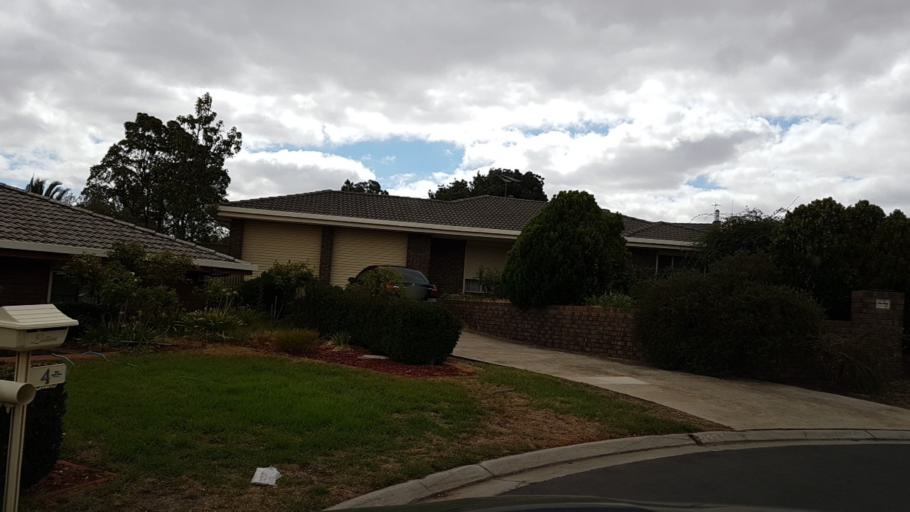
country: AU
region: South Australia
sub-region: Gawler
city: Gawler
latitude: -34.6050
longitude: 138.7611
